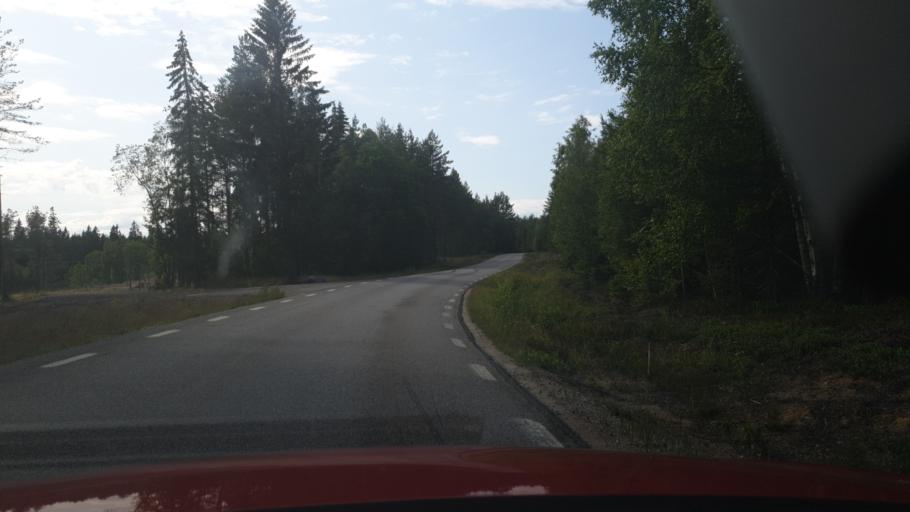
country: SE
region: Vaesternorrland
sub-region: Sundsvalls Kommun
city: Njurundabommen
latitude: 62.0366
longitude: 17.3916
